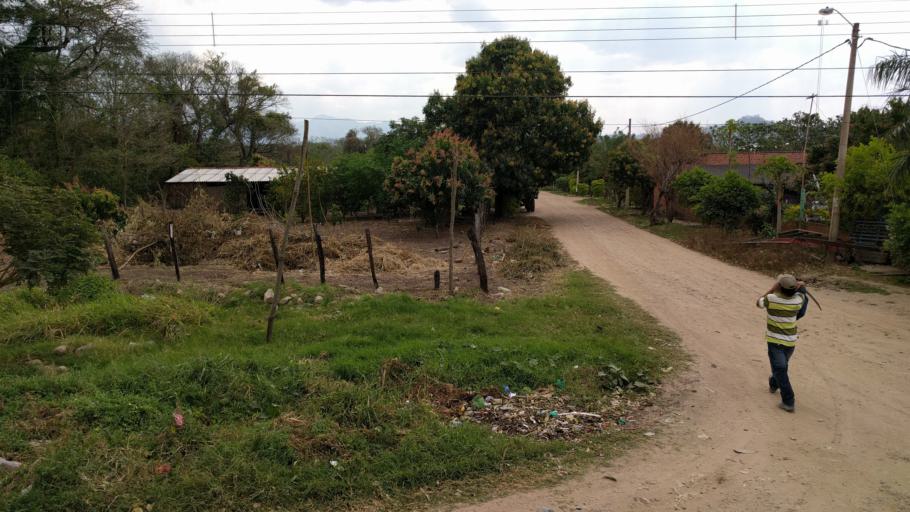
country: BO
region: Santa Cruz
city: Jorochito
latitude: -18.0656
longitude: -63.4363
